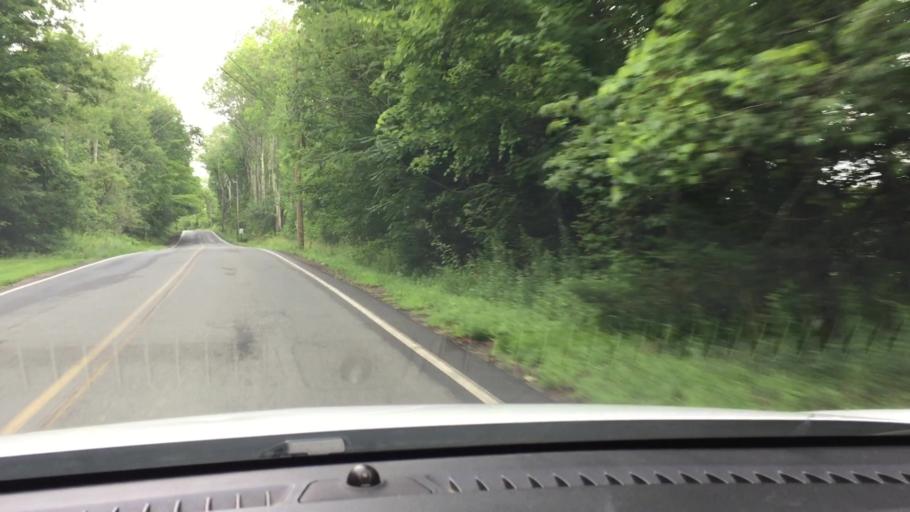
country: US
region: Massachusetts
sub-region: Berkshire County
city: Hinsdale
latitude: 42.4444
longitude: -73.1399
